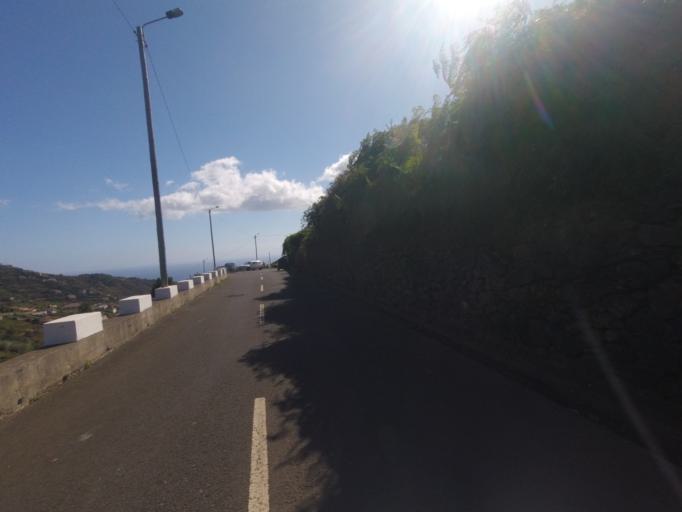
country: PT
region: Madeira
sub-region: Ribeira Brava
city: Campanario
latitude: 32.6771
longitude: -17.0233
